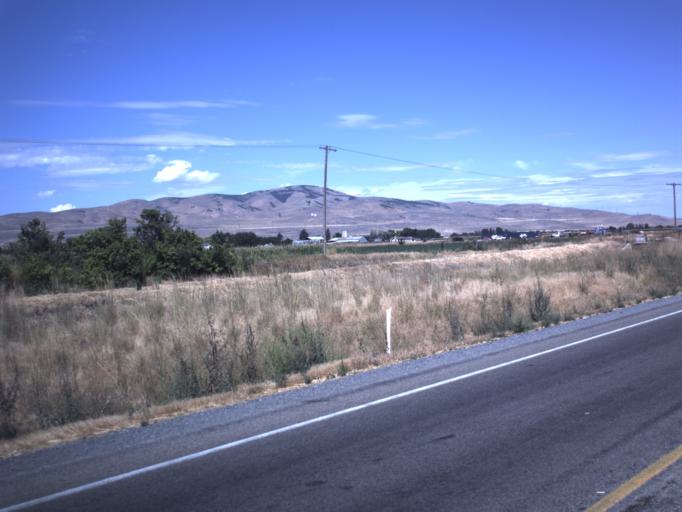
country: US
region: Utah
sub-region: Box Elder County
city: Elwood
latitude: 41.7062
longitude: -112.1420
